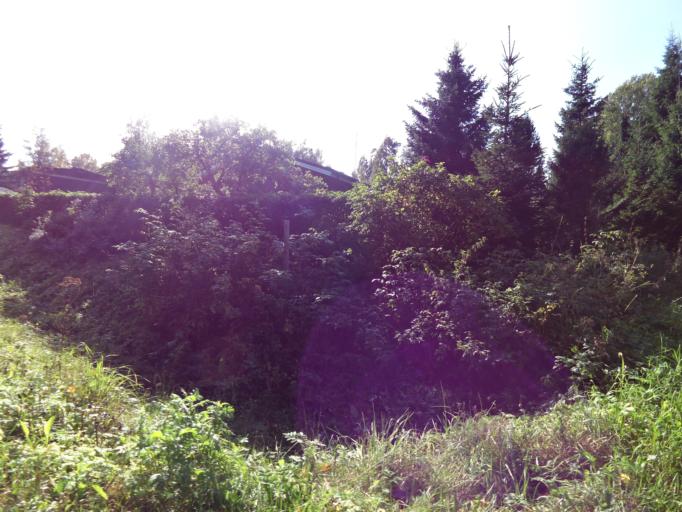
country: FI
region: Uusimaa
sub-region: Helsinki
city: Espoo
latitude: 60.1757
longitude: 24.6548
